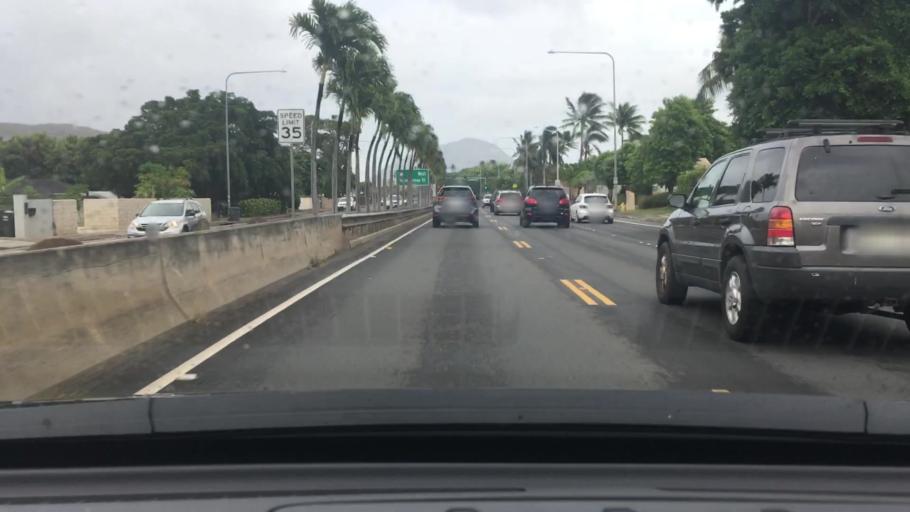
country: US
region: Hawaii
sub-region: Honolulu County
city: Waimanalo Beach
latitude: 21.2805
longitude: -157.7418
